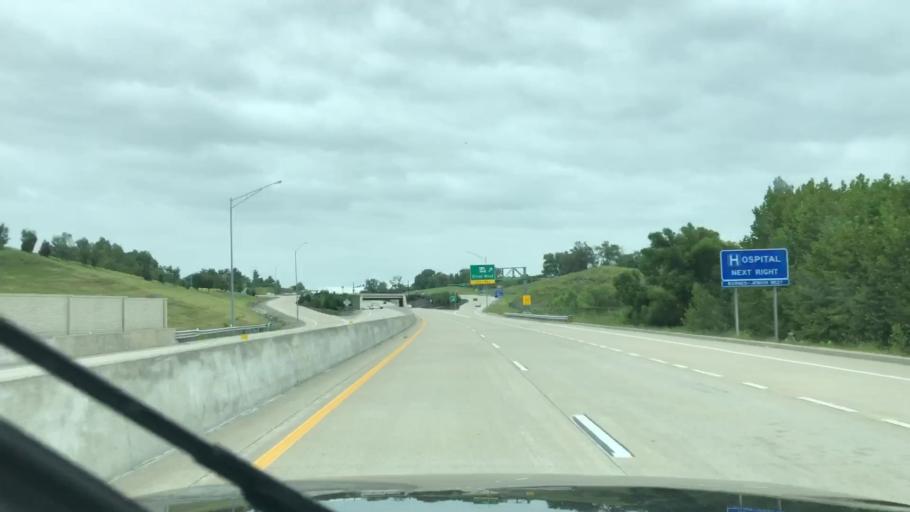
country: US
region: Missouri
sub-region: Saint Louis County
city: Town and Country
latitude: 38.6766
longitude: -90.4934
